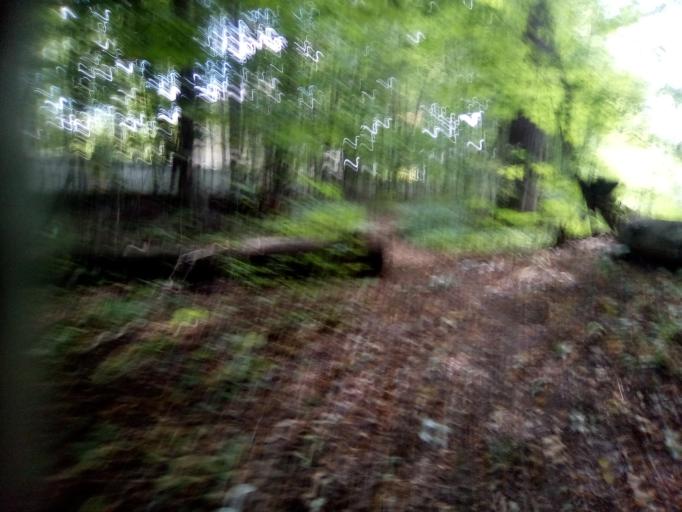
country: RU
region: Moskovskaya
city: Kokoshkino
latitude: 55.6173
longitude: 37.1668
